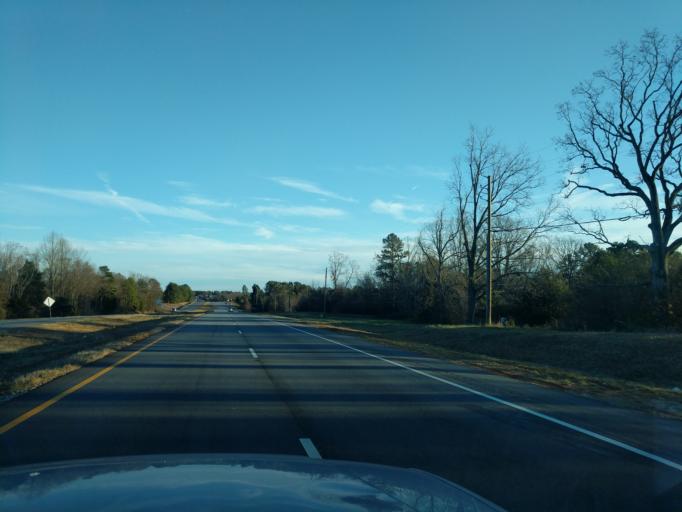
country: US
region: Georgia
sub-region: Franklin County
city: Lavonia
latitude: 34.4687
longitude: -83.1743
